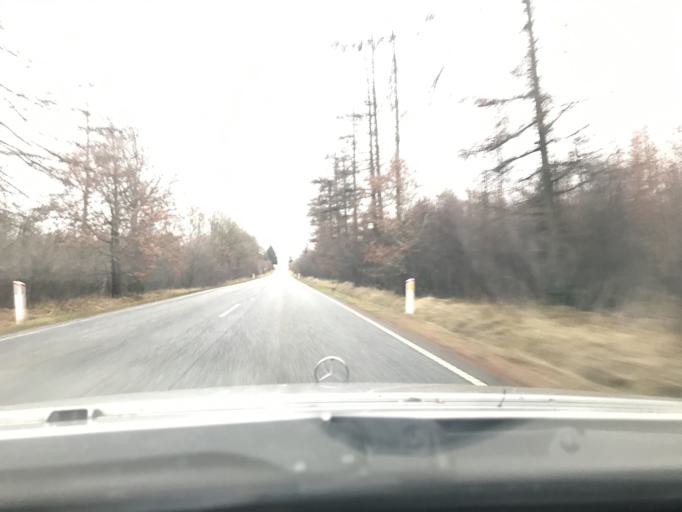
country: DK
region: South Denmark
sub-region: Tonder Kommune
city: Logumkloster
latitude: 55.1740
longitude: 8.9447
